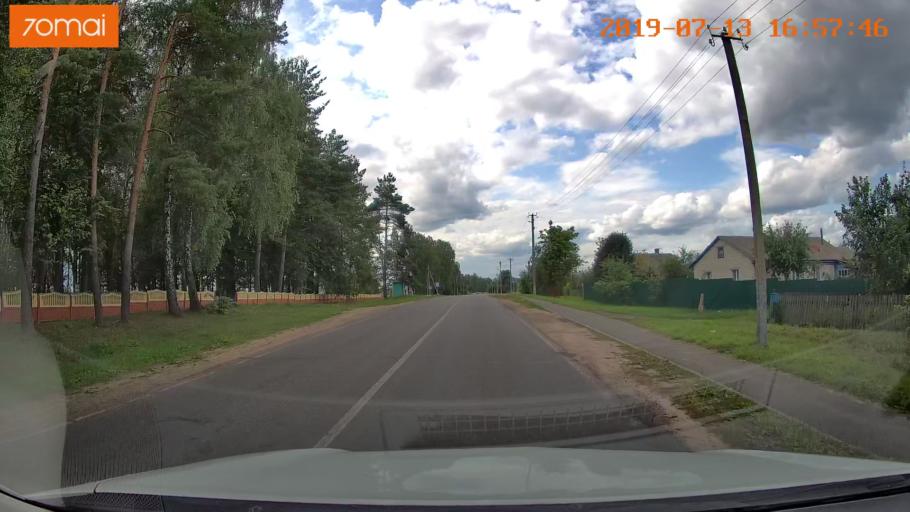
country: BY
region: Mogilev
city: Kirawsk
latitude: 53.2826
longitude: 29.4484
